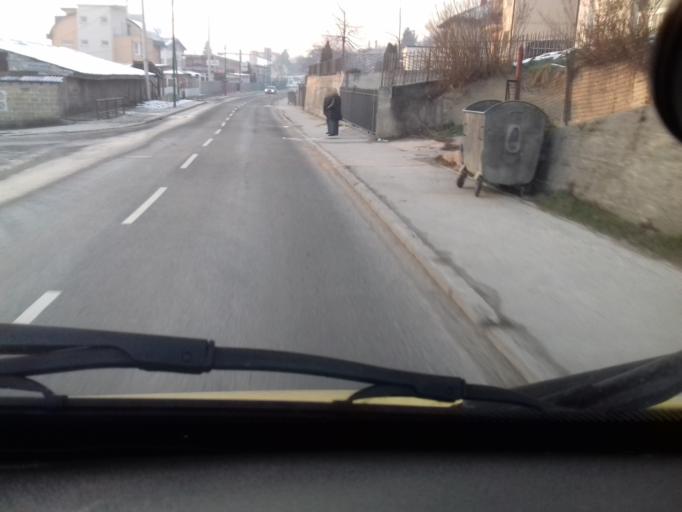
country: BA
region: Federation of Bosnia and Herzegovina
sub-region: Kanton Sarajevo
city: Sarajevo
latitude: 43.8538
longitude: 18.3308
